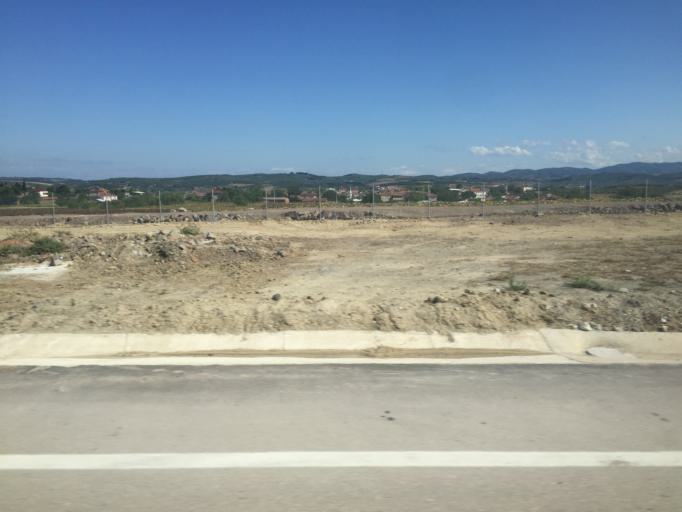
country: TR
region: Bursa
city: Mahmudiye
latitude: 40.2569
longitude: 28.6966
